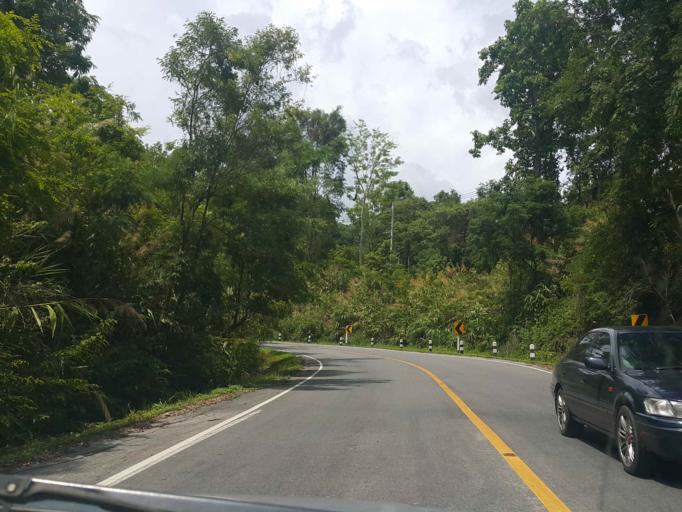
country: TH
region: Nan
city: Ban Luang
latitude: 18.8725
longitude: 100.4841
